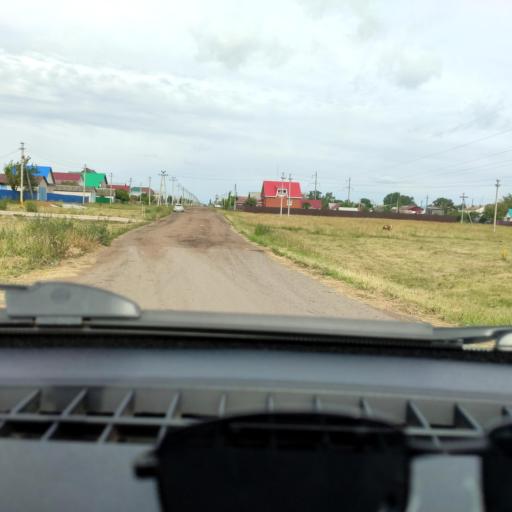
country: RU
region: Bashkortostan
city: Ulukulevo
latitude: 54.4194
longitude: 56.3431
